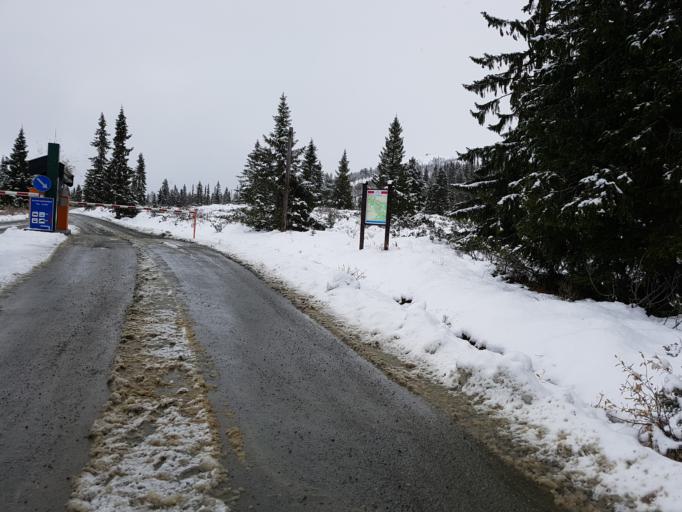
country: NO
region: Oppland
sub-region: Sel
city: Otta
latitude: 61.8070
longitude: 9.6859
